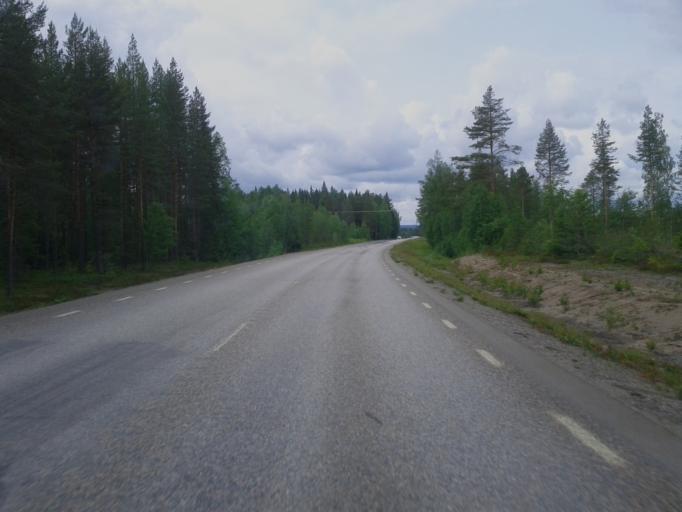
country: SE
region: Vaesterbotten
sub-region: Norsjo Kommun
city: Norsjoe
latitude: 64.9802
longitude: 19.5746
